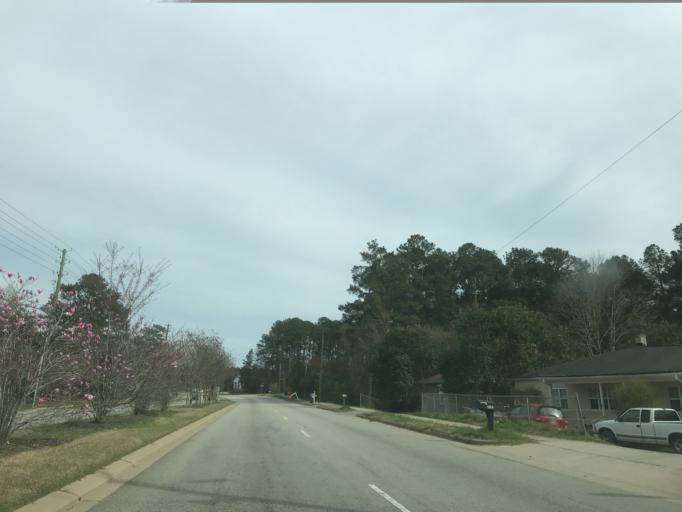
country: US
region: North Carolina
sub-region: Wake County
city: West Raleigh
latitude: 35.7436
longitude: -78.6881
